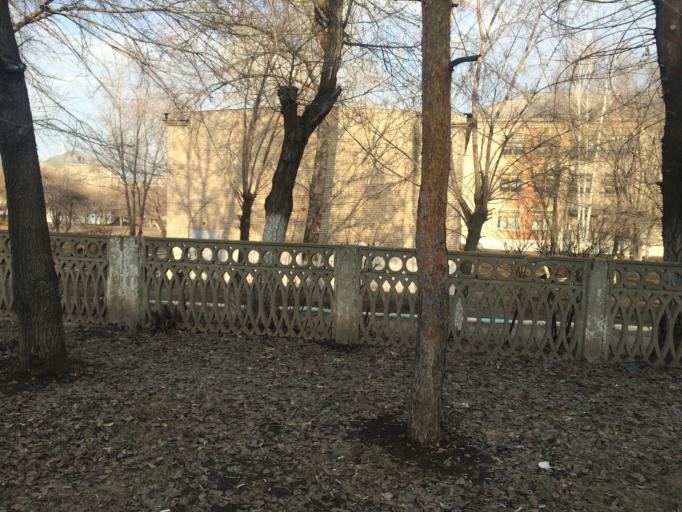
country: RU
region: Chelyabinsk
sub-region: Gorod Magnitogorsk
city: Magnitogorsk
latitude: 53.4011
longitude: 58.9718
